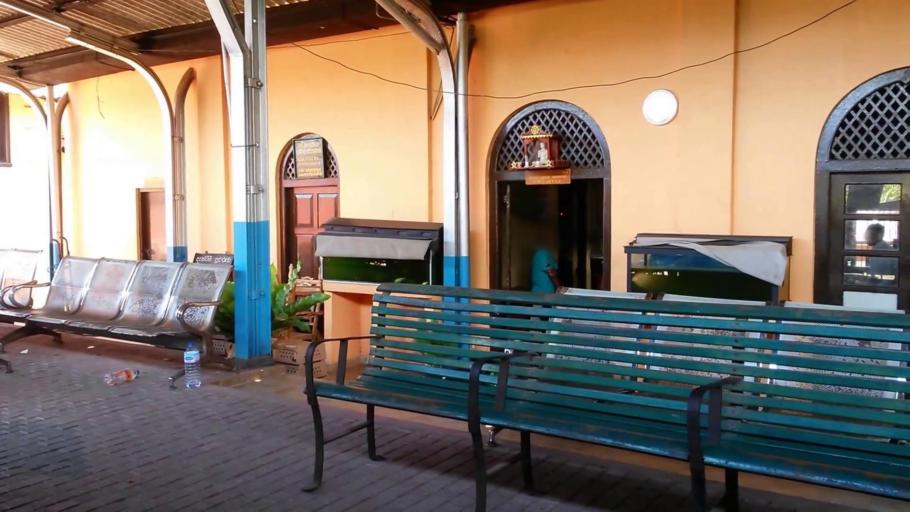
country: LK
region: Southern
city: Hikkaduwa
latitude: 6.1493
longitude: 80.0992
